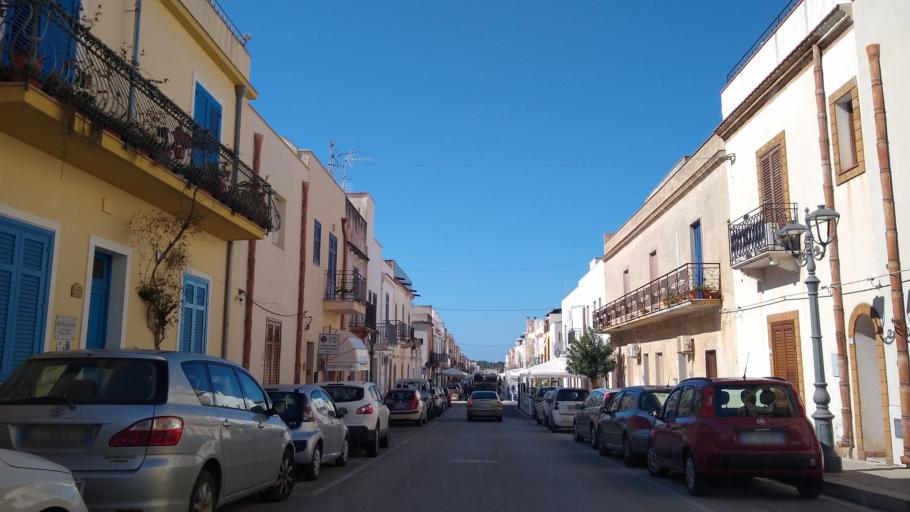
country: IT
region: Sicily
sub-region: Trapani
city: San Vito Lo Capo
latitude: 38.1736
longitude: 12.7339
